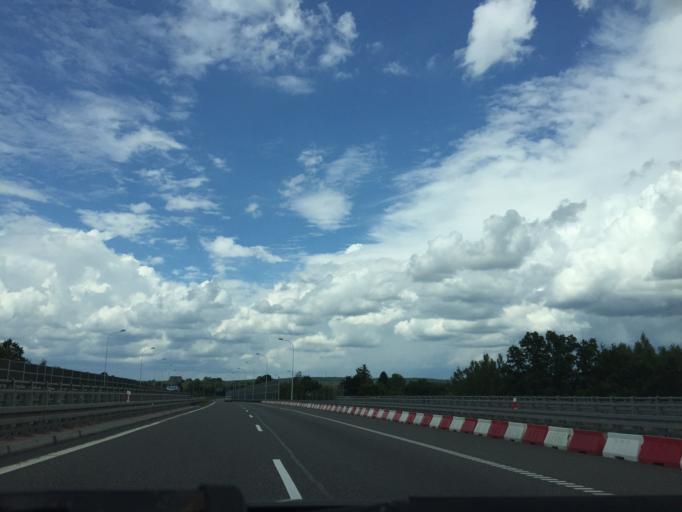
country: PL
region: Swietokrzyskie
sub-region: Powiat skarzyski
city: Skarzysko-Kamienna
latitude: 51.0950
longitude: 20.8358
